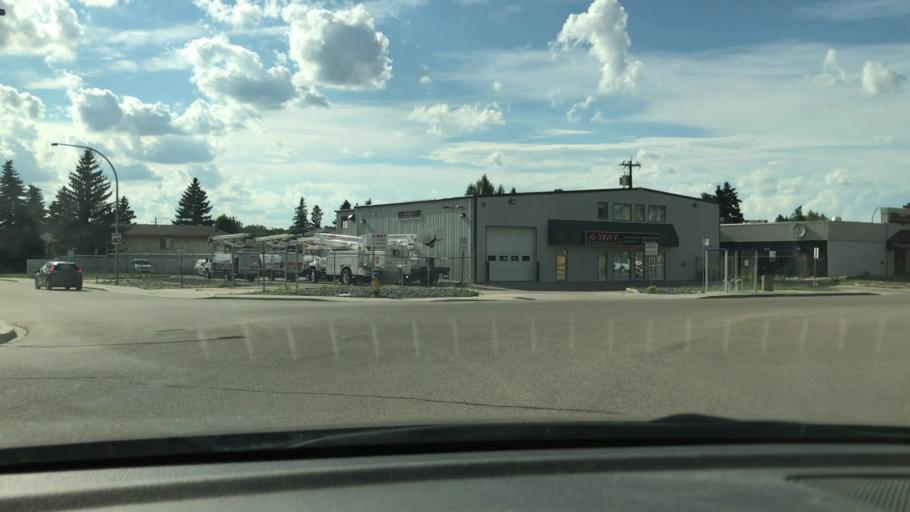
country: CA
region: Alberta
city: Edmonton
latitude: 53.5131
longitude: -113.4366
